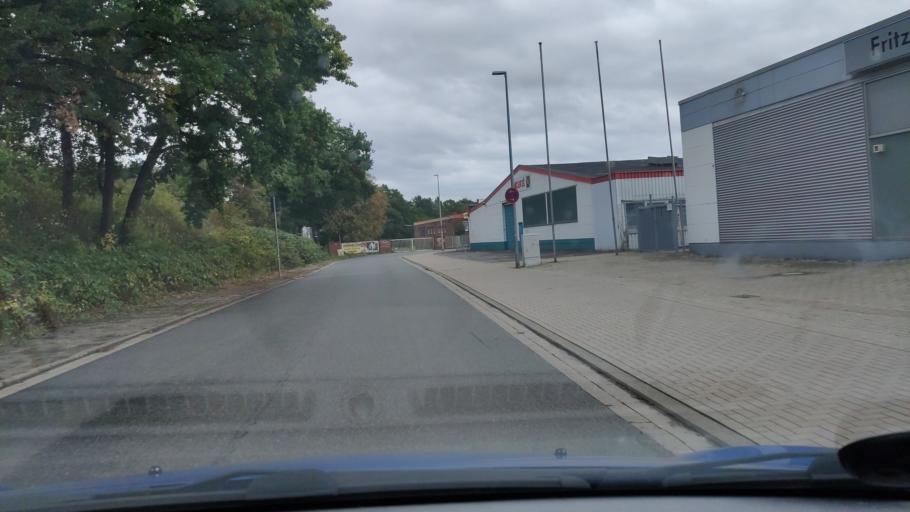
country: DE
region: Lower Saxony
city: Hannover
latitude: 52.3851
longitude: 9.6715
